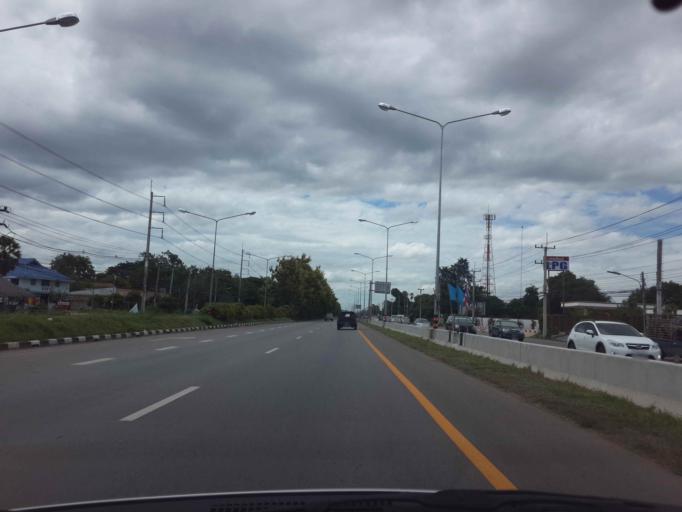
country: TH
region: Phetchaburi
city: Khao Yoi
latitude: 13.1493
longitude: 99.8532
